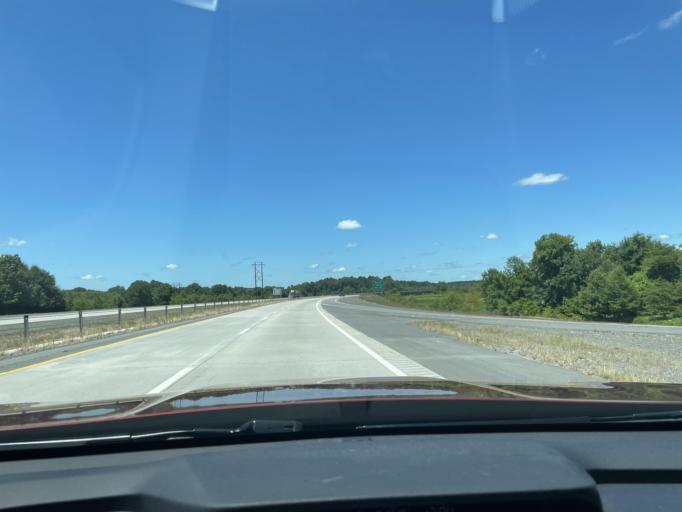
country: US
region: Arkansas
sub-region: Jefferson County
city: Pine Bluff
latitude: 34.1728
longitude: -91.9935
